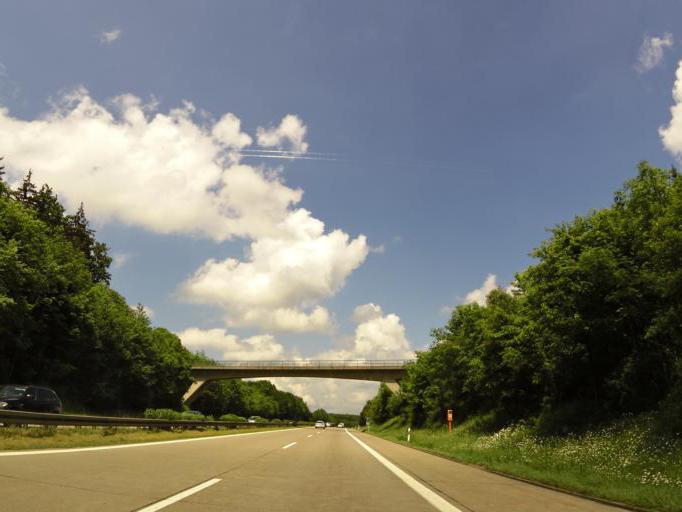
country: DE
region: Baden-Wuerttemberg
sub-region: Regierungsbezirk Stuttgart
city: Nattheim
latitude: 48.7265
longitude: 10.2021
